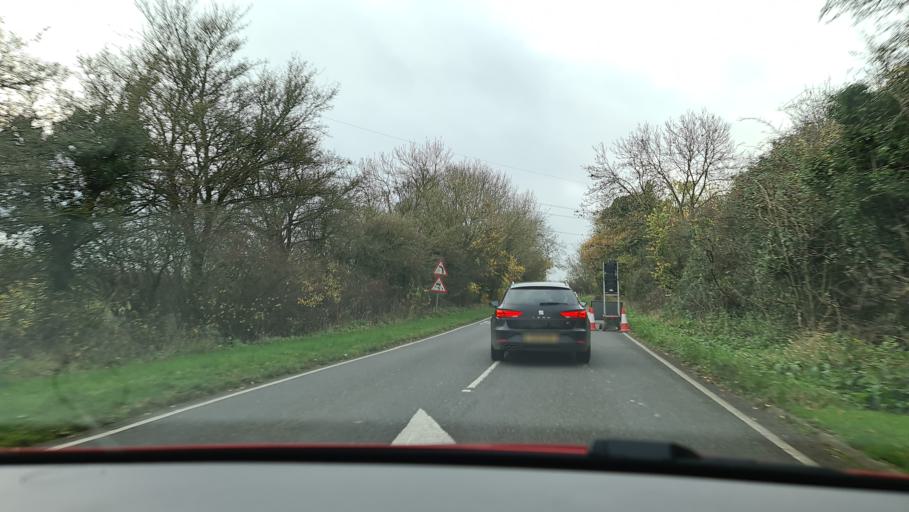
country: GB
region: England
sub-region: Oxfordshire
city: Bicester
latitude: 51.8493
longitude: -1.0900
